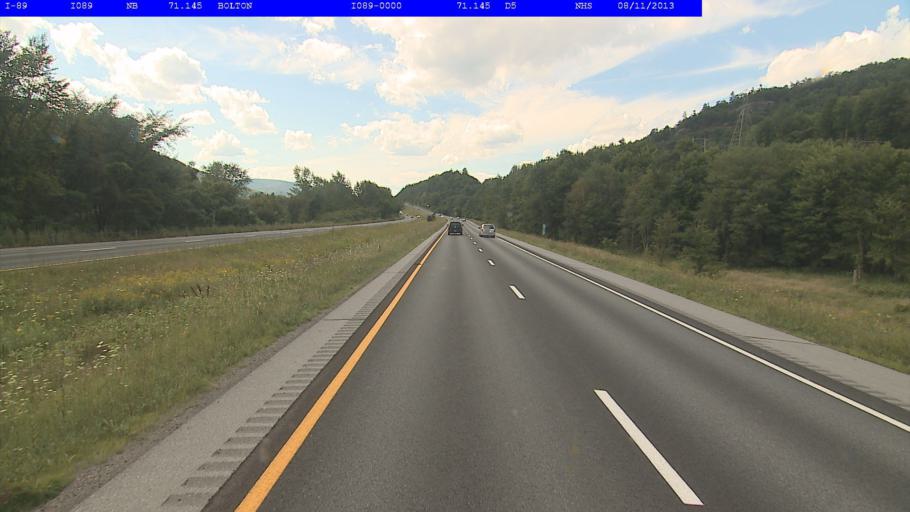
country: US
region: Vermont
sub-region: Washington County
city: Waterbury
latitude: 44.3763
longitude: -72.8895
